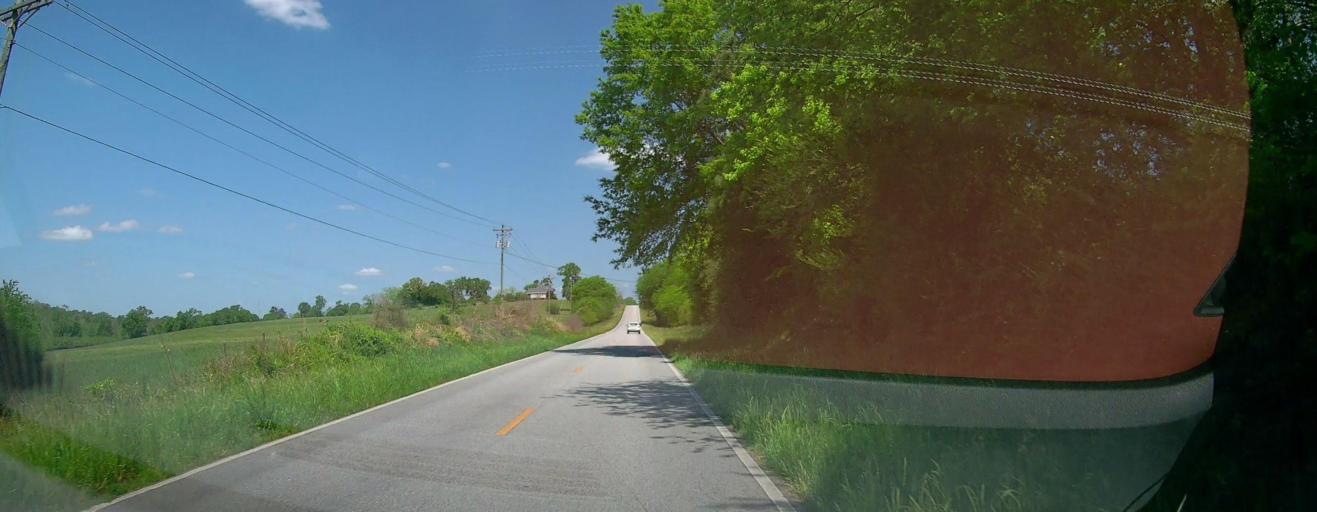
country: US
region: Georgia
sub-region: Bibb County
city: Macon
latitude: 32.9070
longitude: -83.6068
